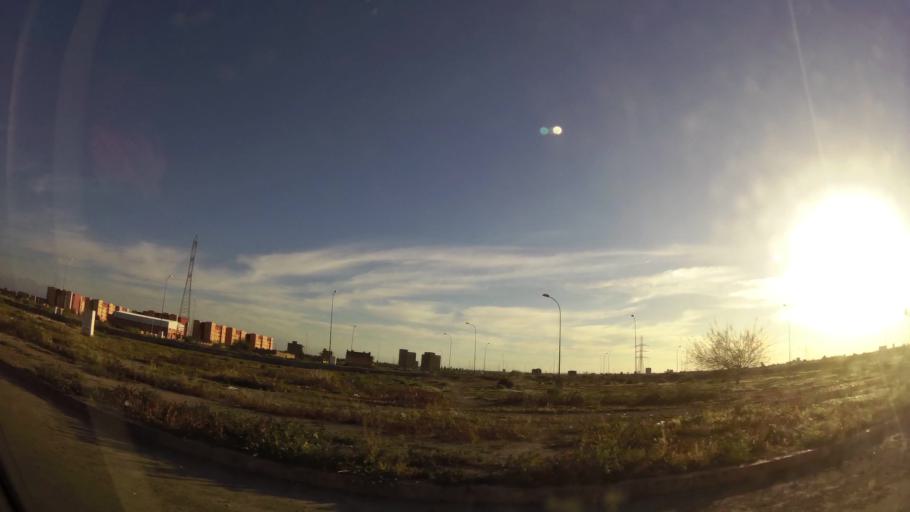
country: MA
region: Marrakech-Tensift-Al Haouz
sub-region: Marrakech
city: Marrakesh
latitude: 31.7448
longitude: -8.1265
